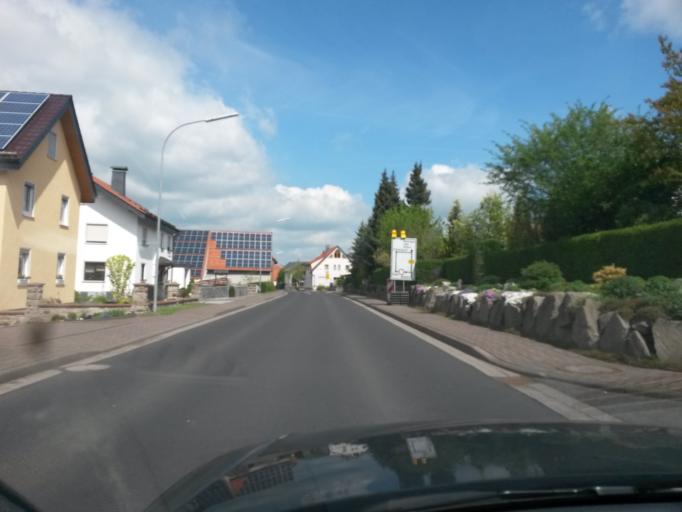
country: DE
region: Hesse
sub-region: Regierungsbezirk Kassel
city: Hilders
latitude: 50.5537
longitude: 10.0107
